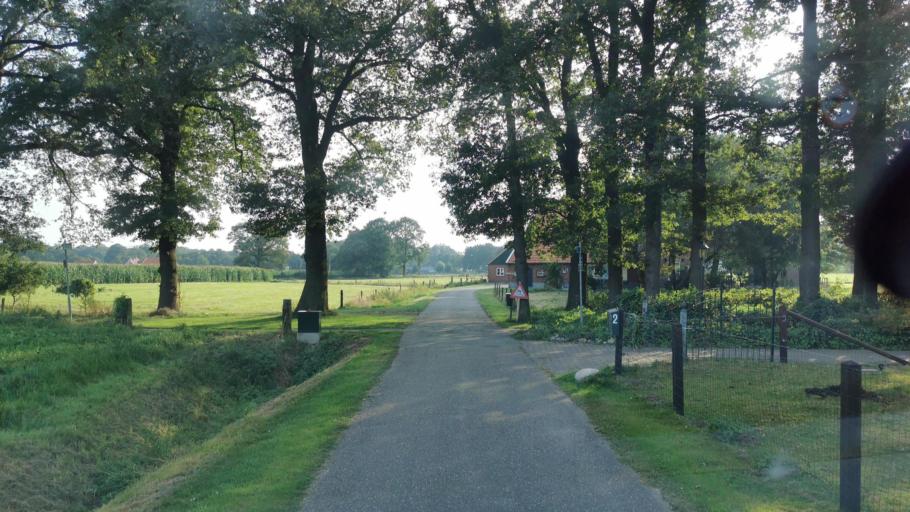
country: NL
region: Overijssel
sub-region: Gemeente Oldenzaal
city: Oldenzaal
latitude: 52.2911
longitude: 6.9515
